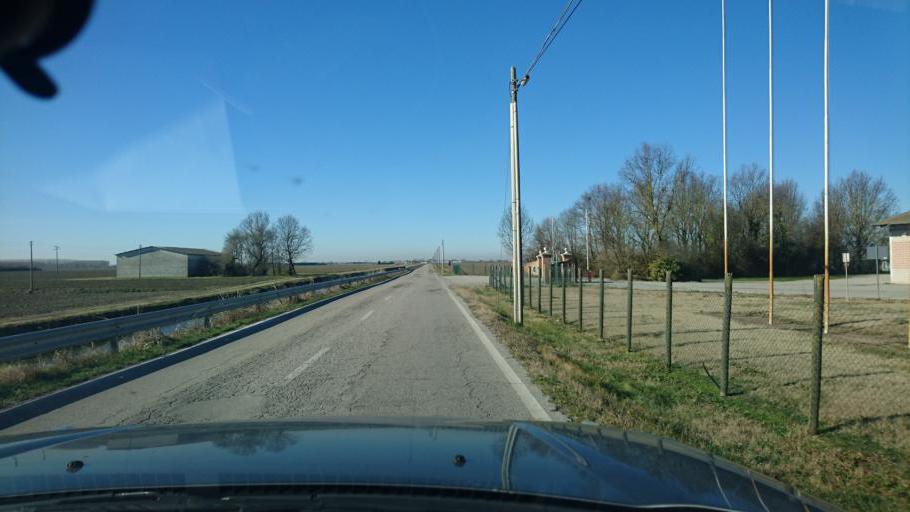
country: IT
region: Emilia-Romagna
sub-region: Provincia di Ferrara
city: Mesola
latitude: 44.9469
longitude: 12.2594
